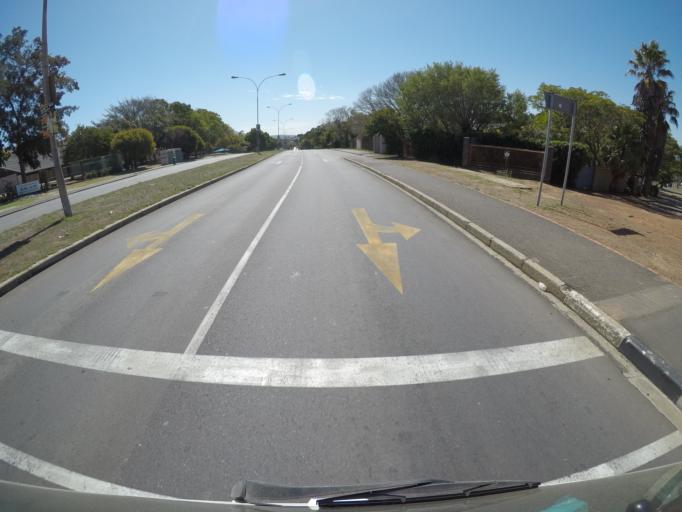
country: ZA
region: Western Cape
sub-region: City of Cape Town
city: Kraaifontein
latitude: -33.8371
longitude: 18.6492
